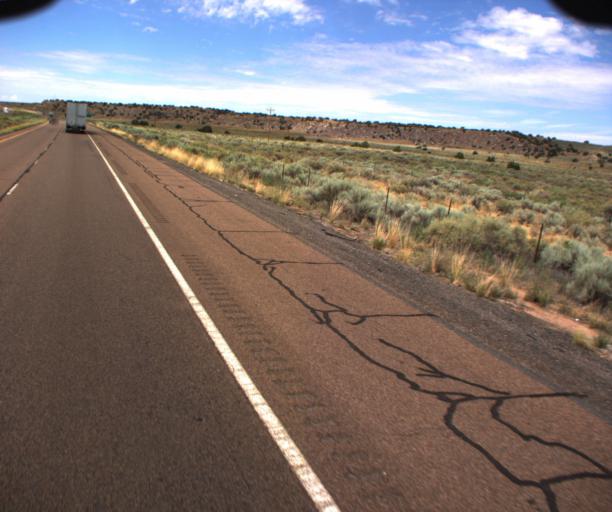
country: US
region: Arizona
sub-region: Apache County
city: Houck
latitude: 35.1873
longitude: -109.4468
